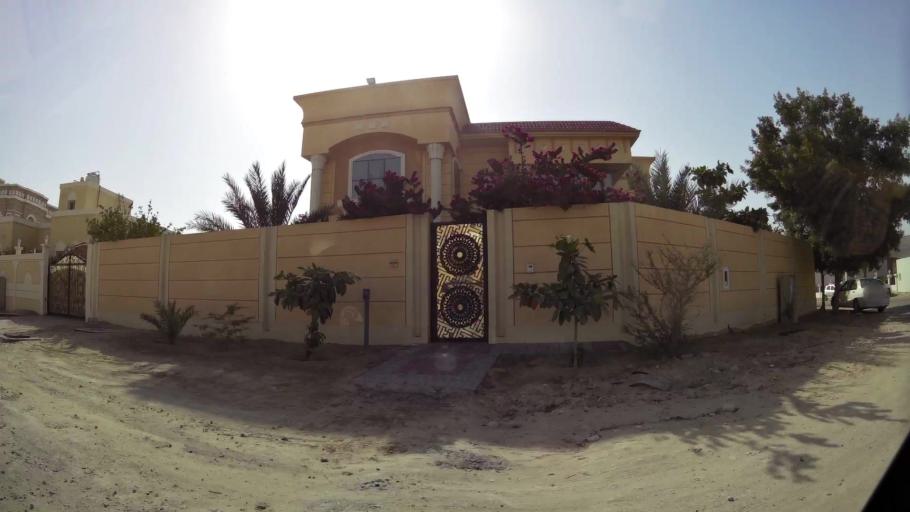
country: AE
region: Dubai
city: Dubai
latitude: 25.1605
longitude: 55.2660
